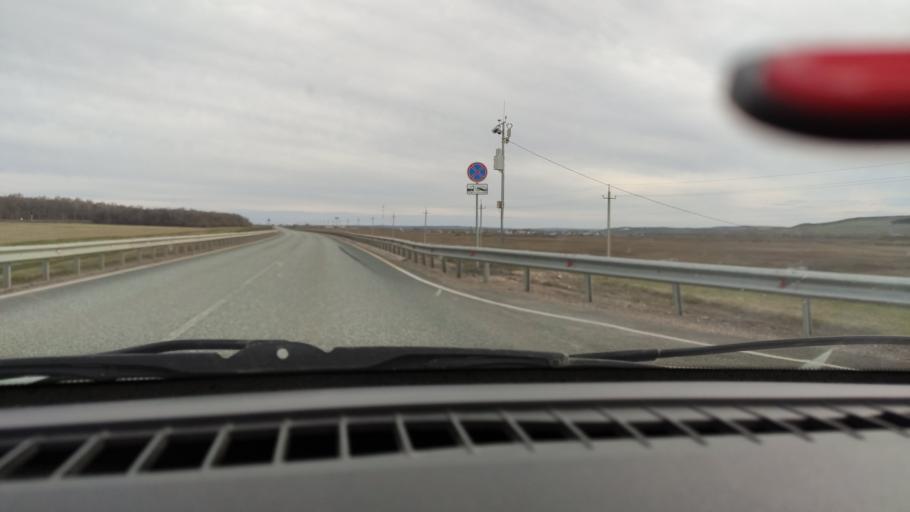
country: RU
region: Bashkortostan
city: Yermolayevo
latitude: 52.5016
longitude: 55.8292
